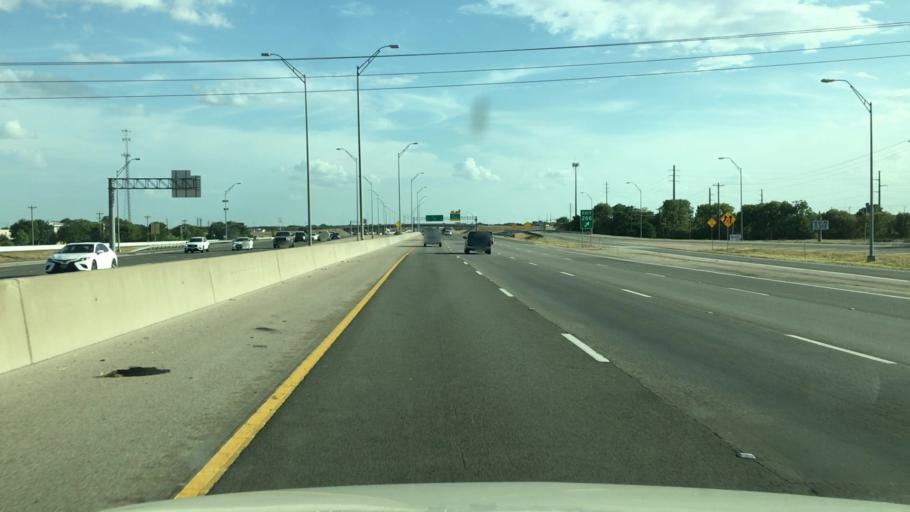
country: US
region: Texas
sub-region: Williamson County
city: Serenada
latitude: 30.7086
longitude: -97.6496
